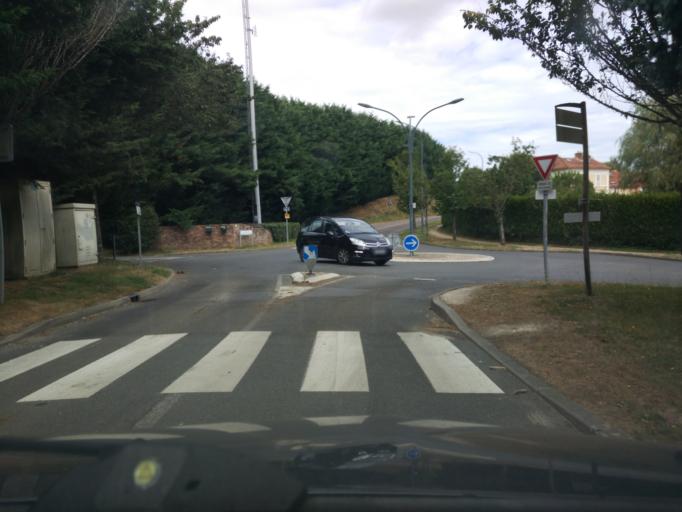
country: FR
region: Ile-de-France
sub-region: Departement de l'Essonne
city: Villiers-le-Bacle
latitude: 48.7089
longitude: 2.1204
